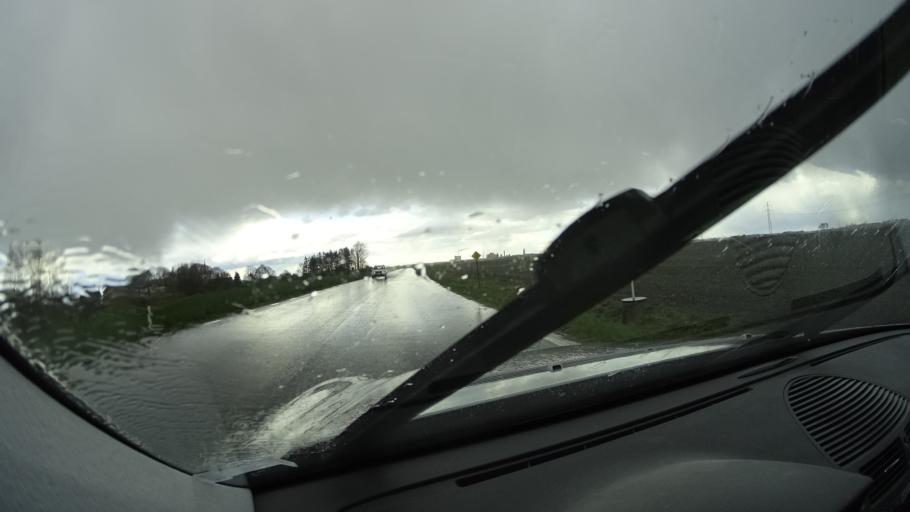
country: SE
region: Skane
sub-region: Lunds Kommun
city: Lund
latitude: 55.7708
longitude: 13.2248
